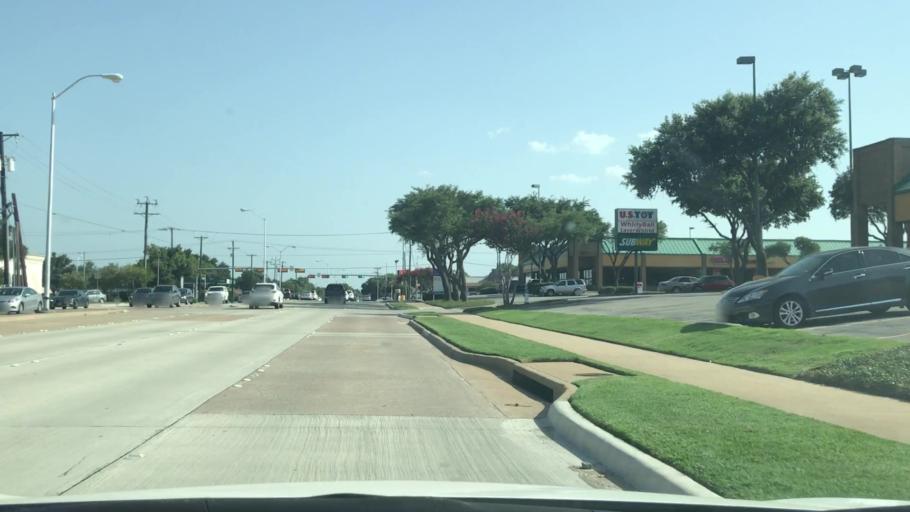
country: US
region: Texas
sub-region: Collin County
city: Plano
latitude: 33.0426
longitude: -96.7534
